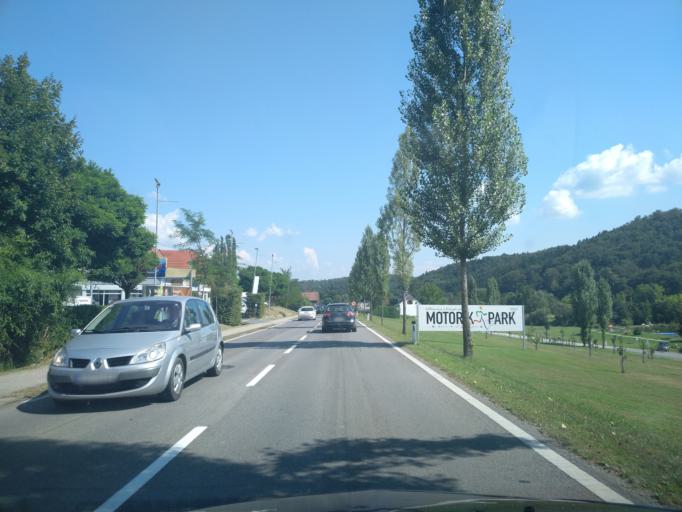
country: AT
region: Styria
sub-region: Politischer Bezirk Leibnitz
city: Retznei
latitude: 46.7212
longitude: 15.5665
